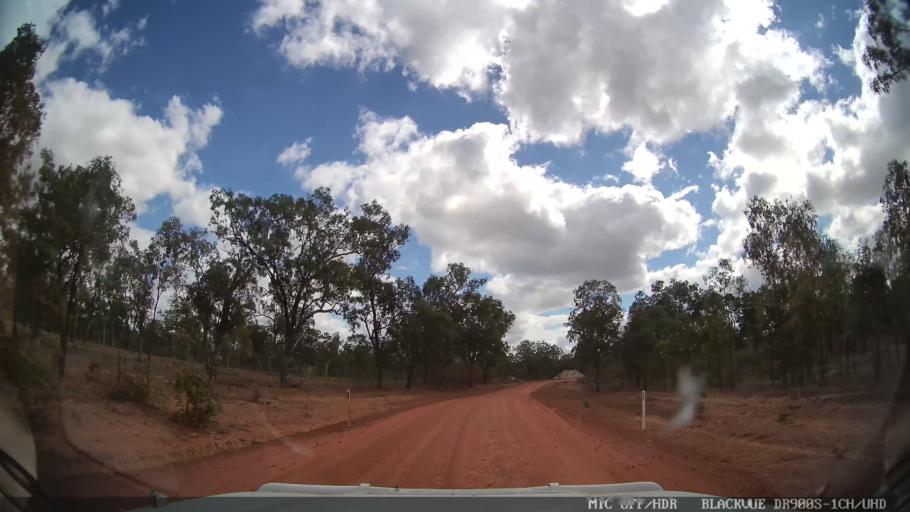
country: AU
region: Queensland
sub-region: Cook
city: Cooktown
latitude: -15.3523
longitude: 144.4600
